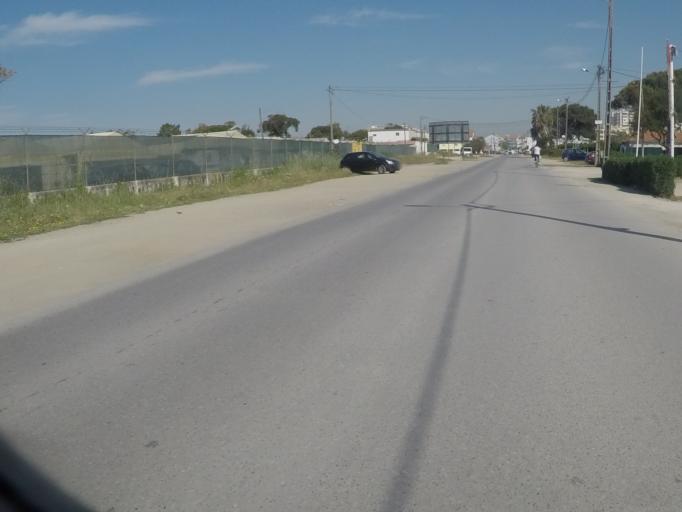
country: PT
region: Setubal
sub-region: Almada
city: Costa de Caparica
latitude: 38.6342
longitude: -9.2263
